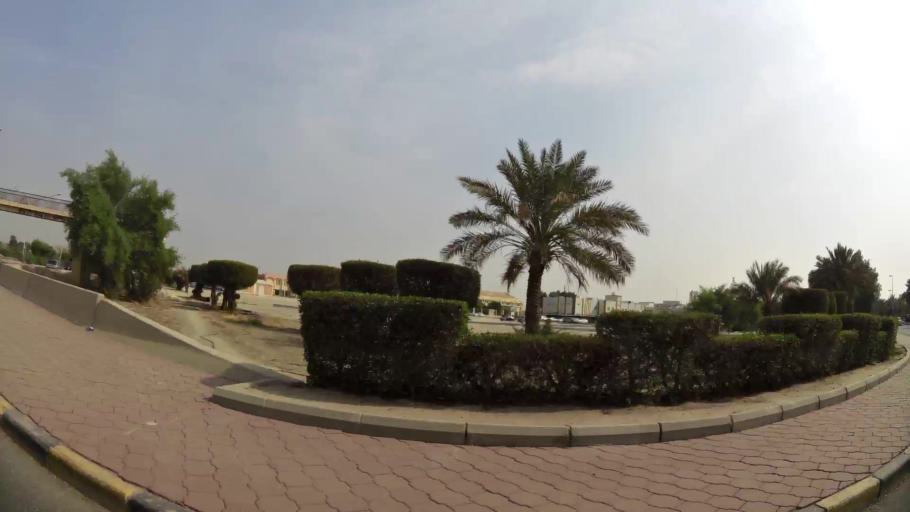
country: KW
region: Al Asimah
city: Ar Rabiyah
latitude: 29.2887
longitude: 47.9384
